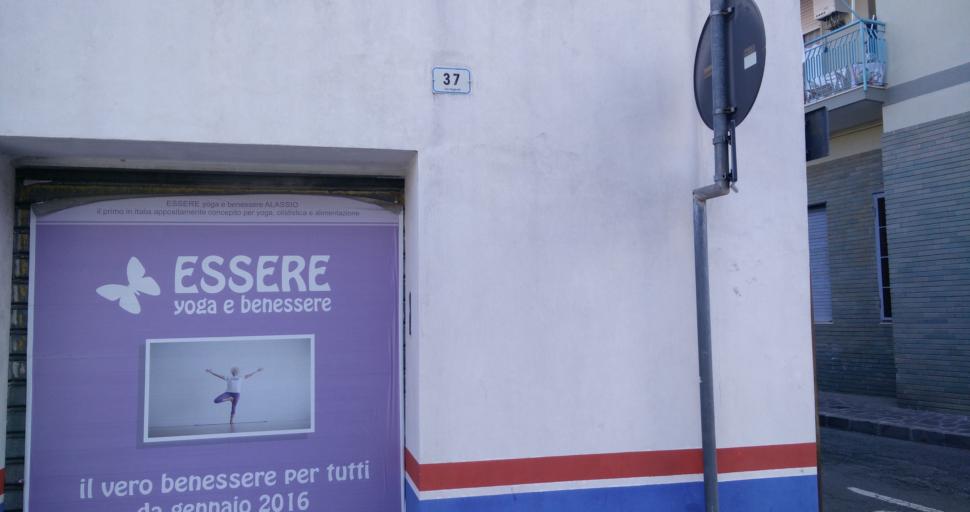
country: IT
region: Liguria
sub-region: Provincia di Savona
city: Alassio
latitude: 44.0022
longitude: 8.1622
